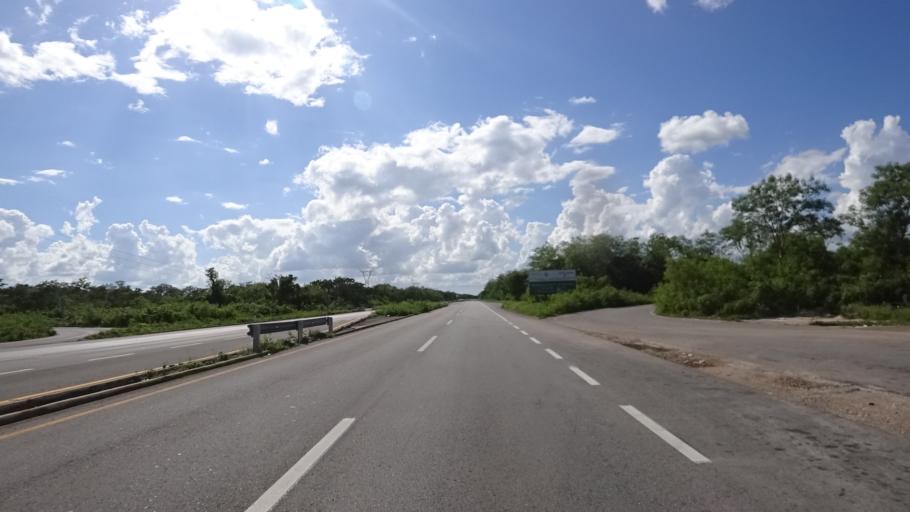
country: MX
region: Yucatan
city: Hoctun
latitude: 20.8764
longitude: -89.2004
